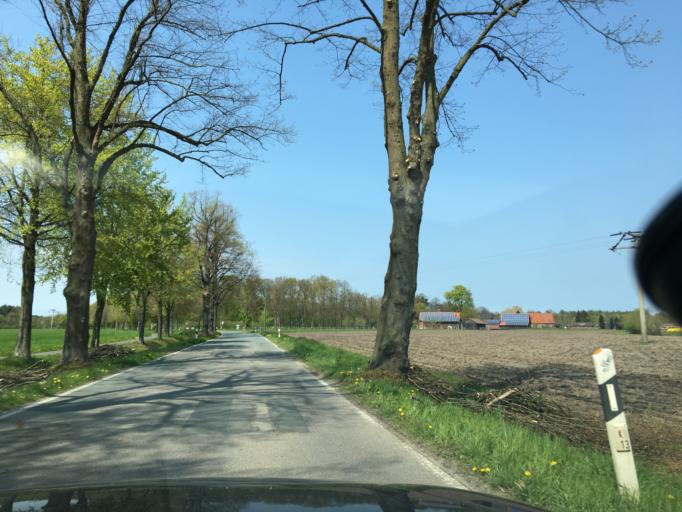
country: DE
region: North Rhine-Westphalia
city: Ludinghausen
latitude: 51.7850
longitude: 7.4345
